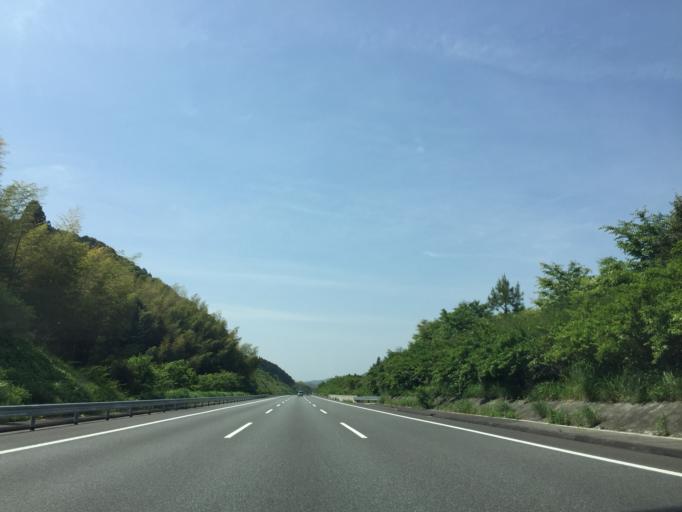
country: JP
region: Shizuoka
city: Fujieda
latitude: 34.9380
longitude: 138.2783
